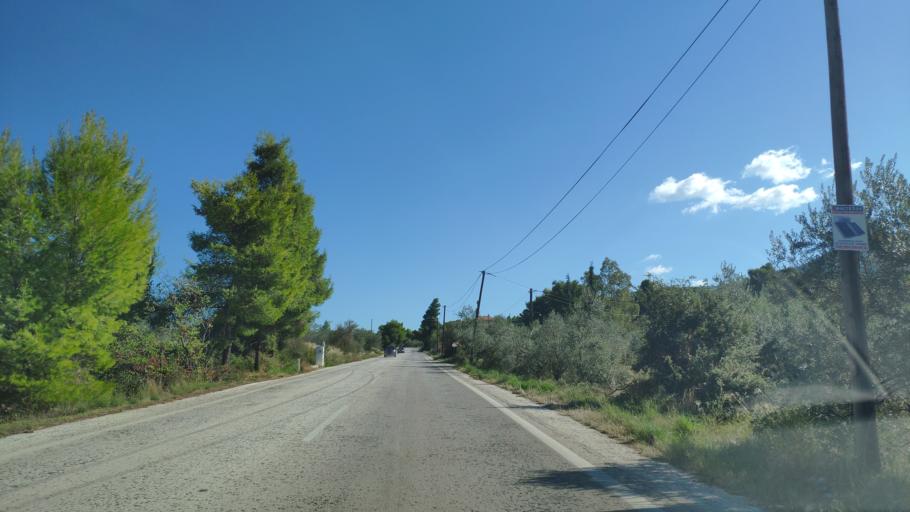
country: GR
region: Peloponnese
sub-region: Nomos Korinthias
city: Loutra Oraias Elenis
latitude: 37.8367
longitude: 23.0089
